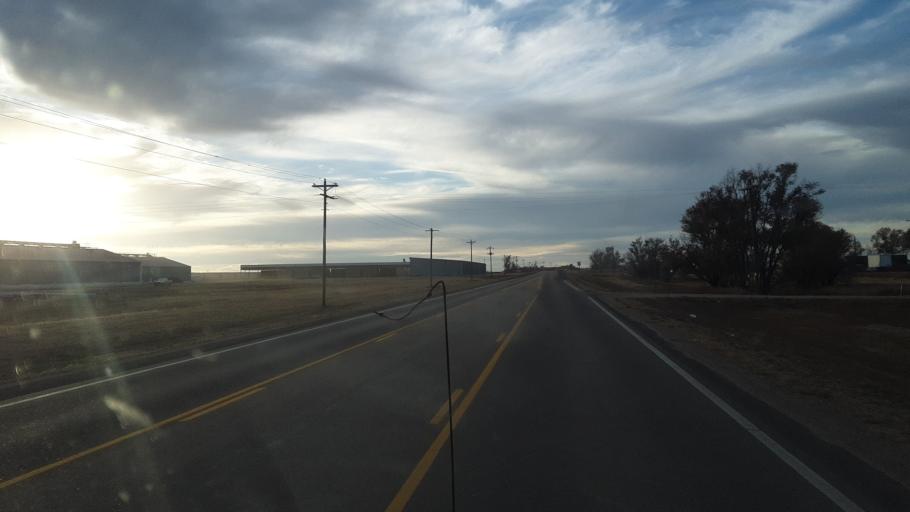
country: US
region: Kansas
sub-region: Hamilton County
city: Syracuse
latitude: 38.0412
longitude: -102.0135
